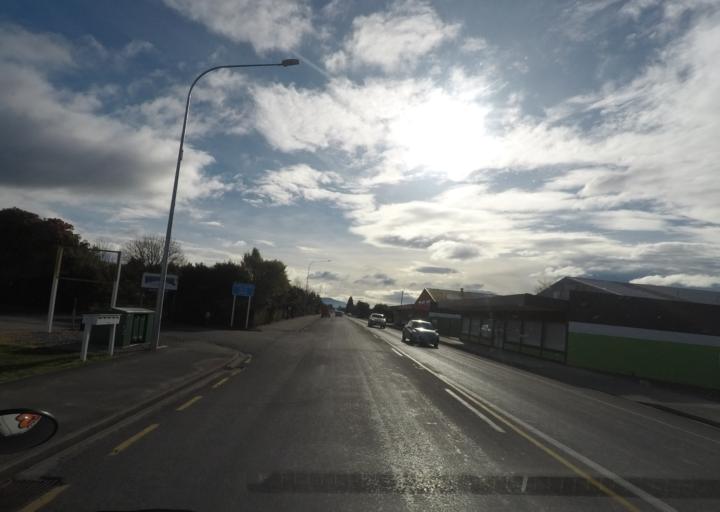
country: NZ
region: Tasman
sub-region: Tasman District
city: Motueka
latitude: -41.1233
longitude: 173.0105
